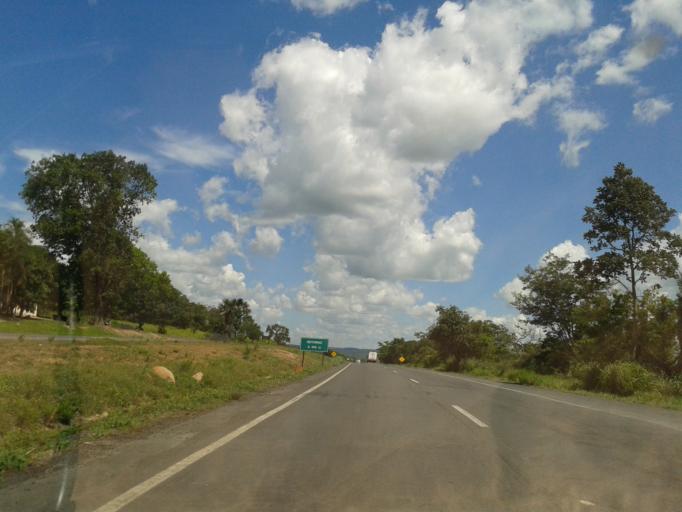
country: BR
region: Goias
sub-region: Piracanjuba
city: Piracanjuba
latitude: -17.3719
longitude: -49.2428
